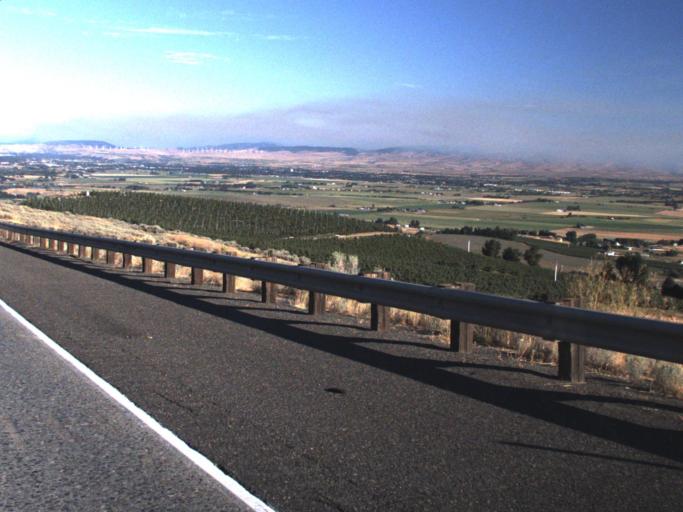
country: US
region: Washington
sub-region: Kittitas County
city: Kittitas
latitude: 46.9036
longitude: -120.4557
